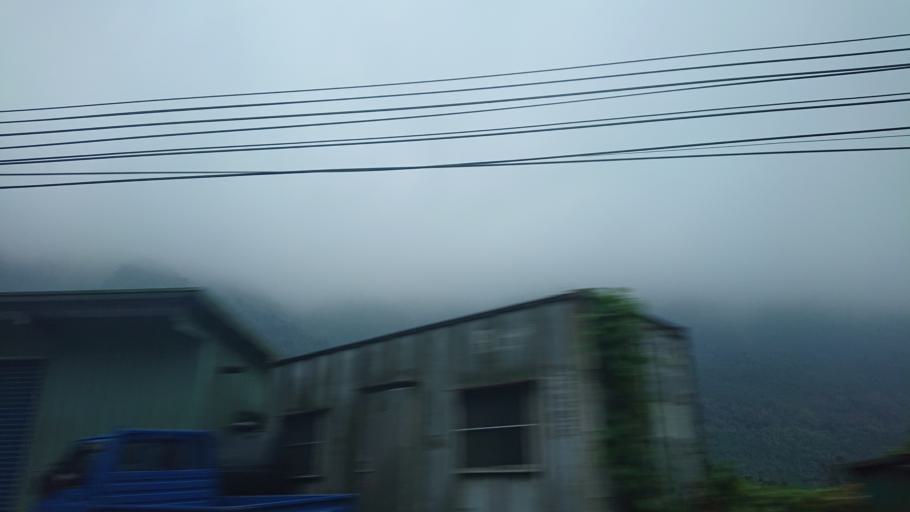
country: TW
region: Taiwan
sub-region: Chiayi
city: Jiayi Shi
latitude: 23.4779
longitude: 120.7141
